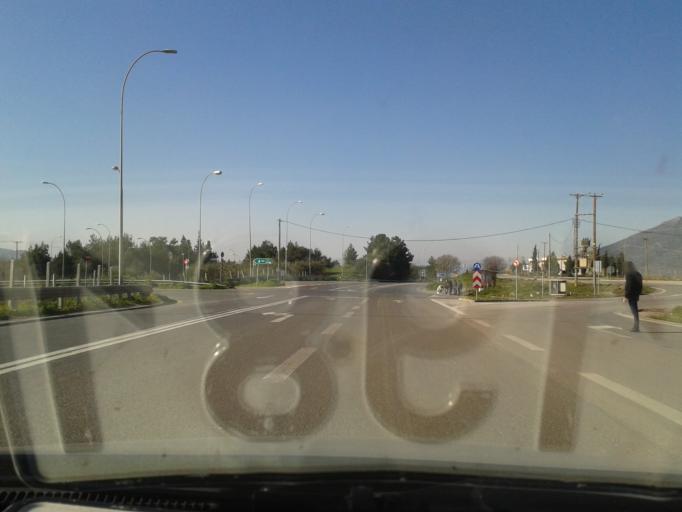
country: GR
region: Central Greece
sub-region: Nomos Voiotias
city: Arma
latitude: 38.3806
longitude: 23.4909
